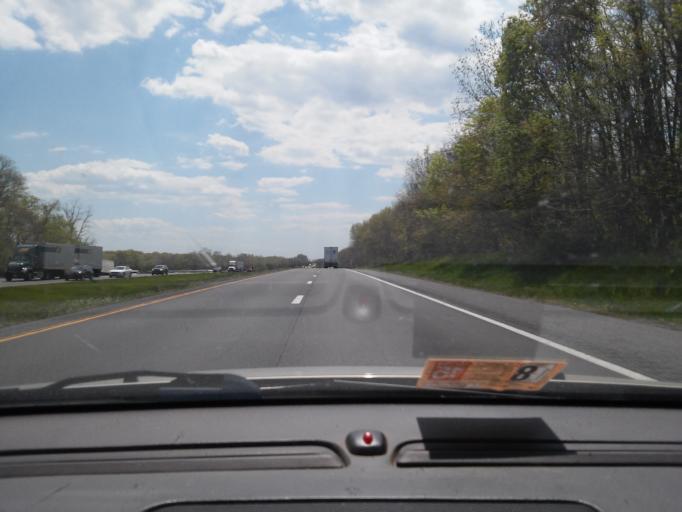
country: US
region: West Virginia
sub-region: Berkeley County
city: Inwood
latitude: 39.3240
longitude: -78.0707
